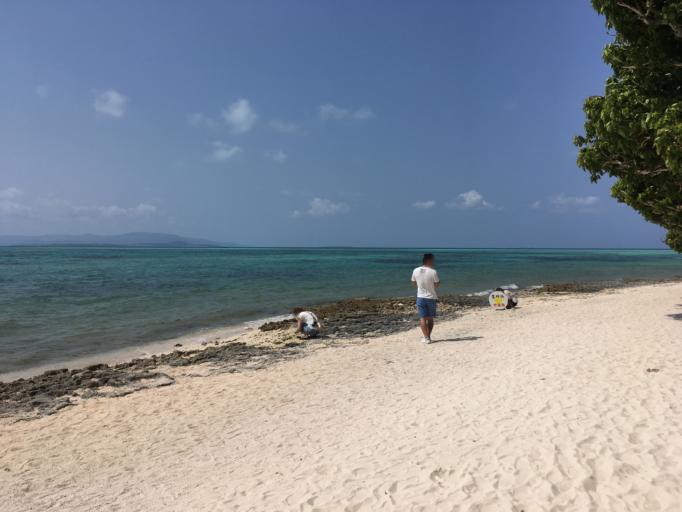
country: JP
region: Okinawa
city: Ishigaki
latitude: 24.3203
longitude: 124.0769
